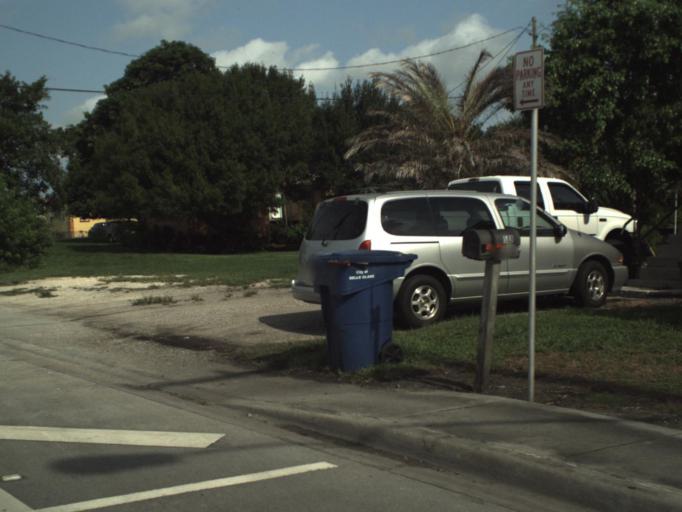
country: US
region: Florida
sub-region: Palm Beach County
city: Belle Glade
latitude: 26.6823
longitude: -80.6624
